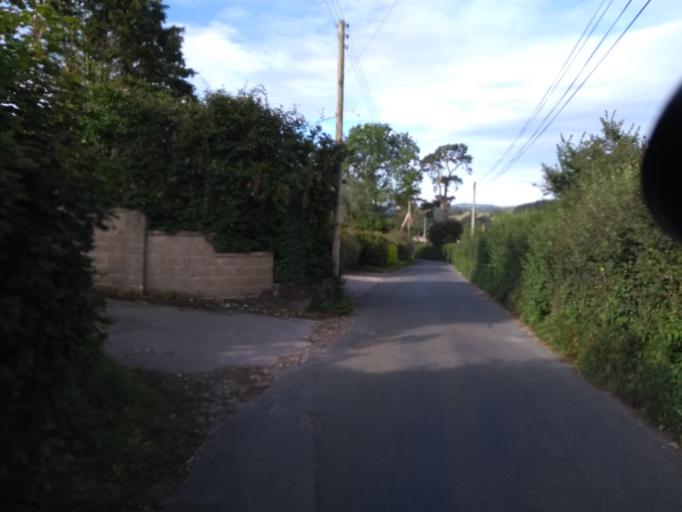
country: GB
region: England
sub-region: Dorset
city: Beaminster
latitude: 50.8139
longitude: -2.7277
